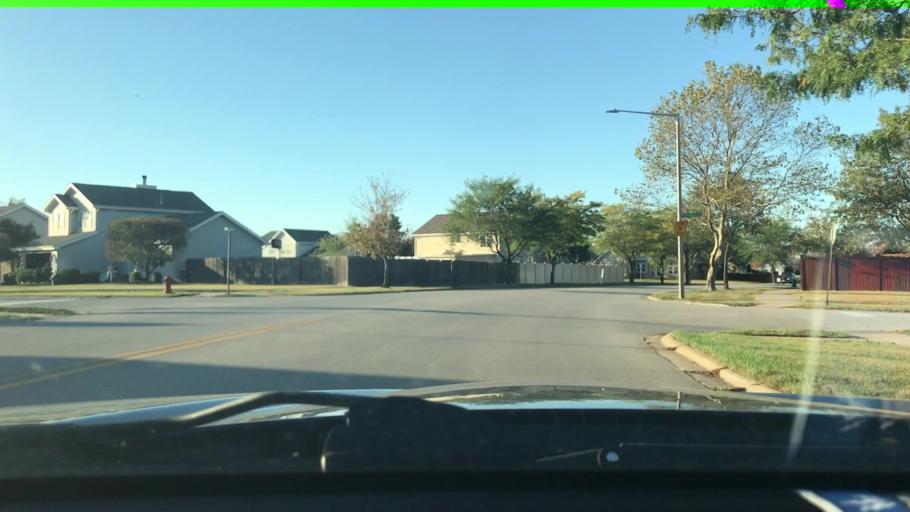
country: US
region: Illinois
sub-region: Will County
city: Frankfort Square
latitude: 41.5180
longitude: -87.8111
